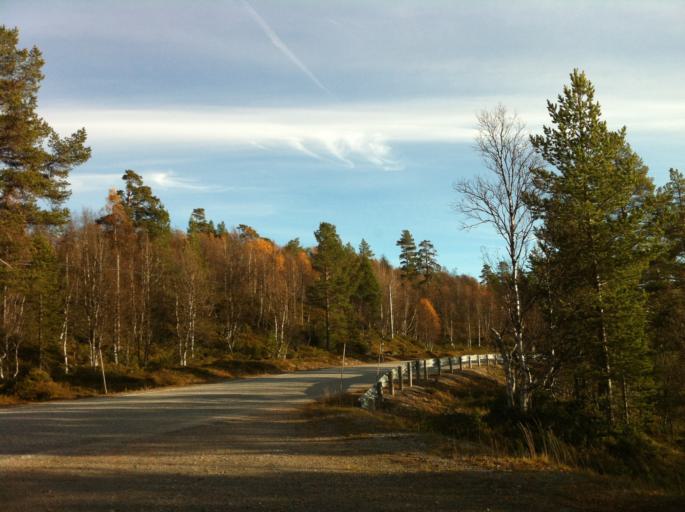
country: NO
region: Hedmark
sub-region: Engerdal
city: Engerdal
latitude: 62.1132
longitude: 12.0175
